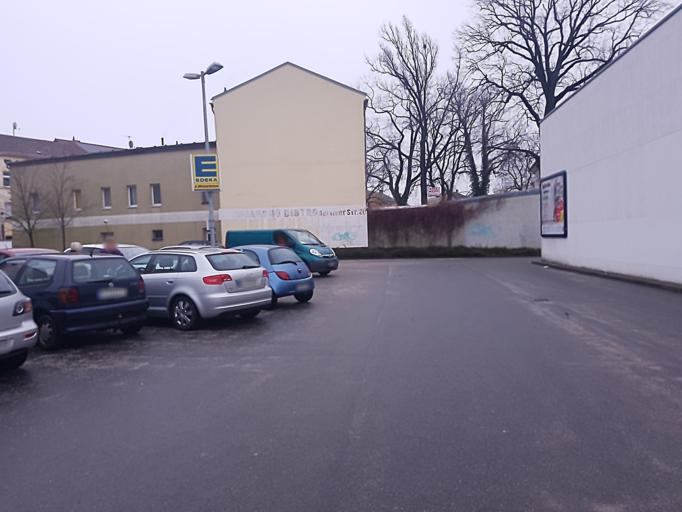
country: DE
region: Brandenburg
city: Finsterwalde
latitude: 51.6348
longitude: 13.7074
